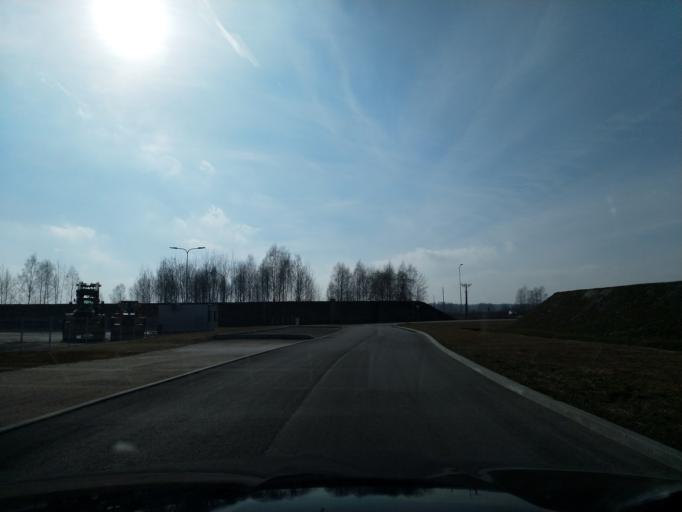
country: LV
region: Kuldigas Rajons
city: Kuldiga
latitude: 56.9555
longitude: 21.9826
